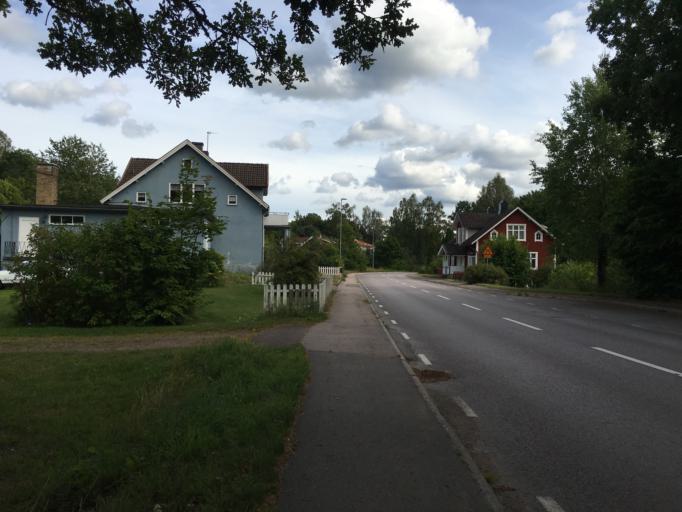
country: SE
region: Kalmar
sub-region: Nybro Kommun
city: Nybro
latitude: 56.9448
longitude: 15.9128
